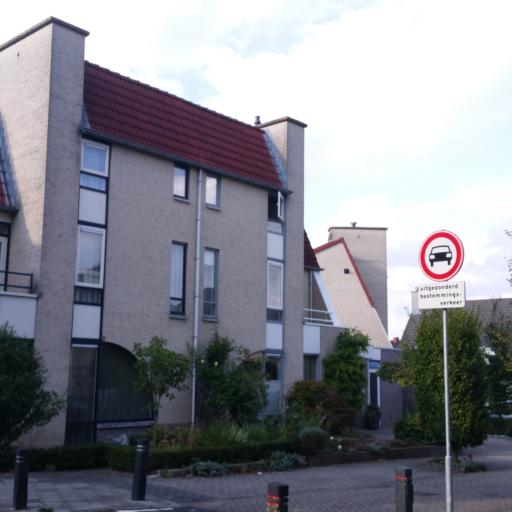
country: NL
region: Utrecht
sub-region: Gemeente IJsselstein
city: IJsselstein
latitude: 52.0235
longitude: 5.0420
